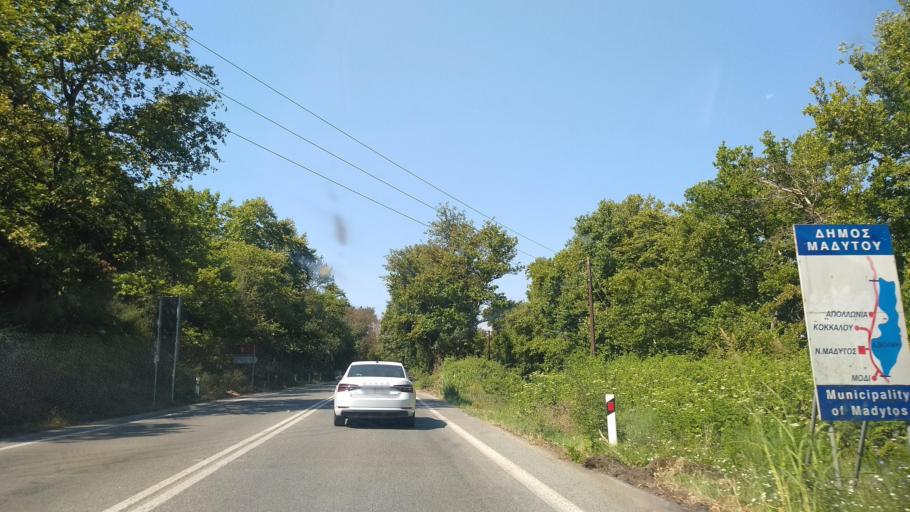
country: GR
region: Central Macedonia
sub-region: Nomos Thessalonikis
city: Stavros
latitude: 40.6557
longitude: 23.6140
